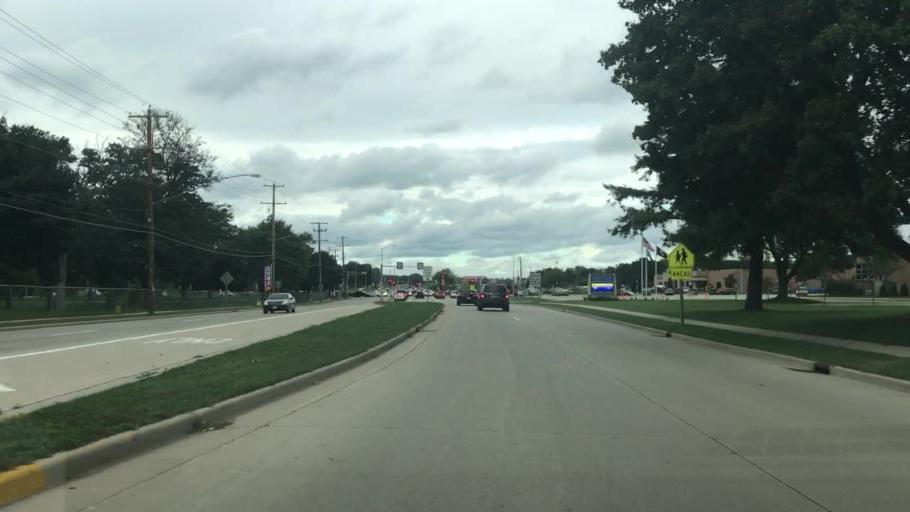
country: US
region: Wisconsin
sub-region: Waukesha County
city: Mukwonago
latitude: 42.8723
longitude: -88.3369
